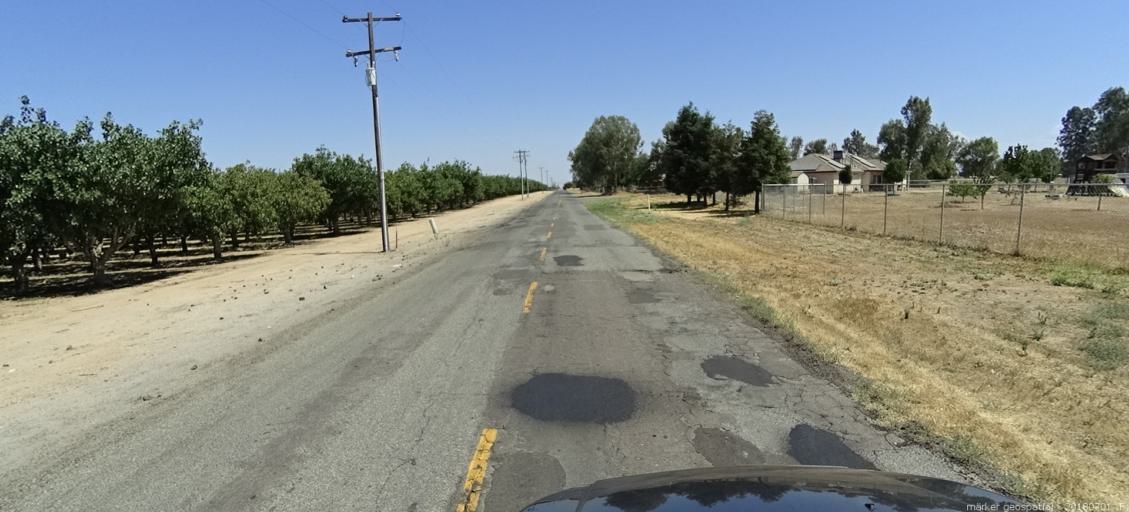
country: US
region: California
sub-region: Madera County
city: Madera Acres
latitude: 37.0605
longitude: -120.0293
